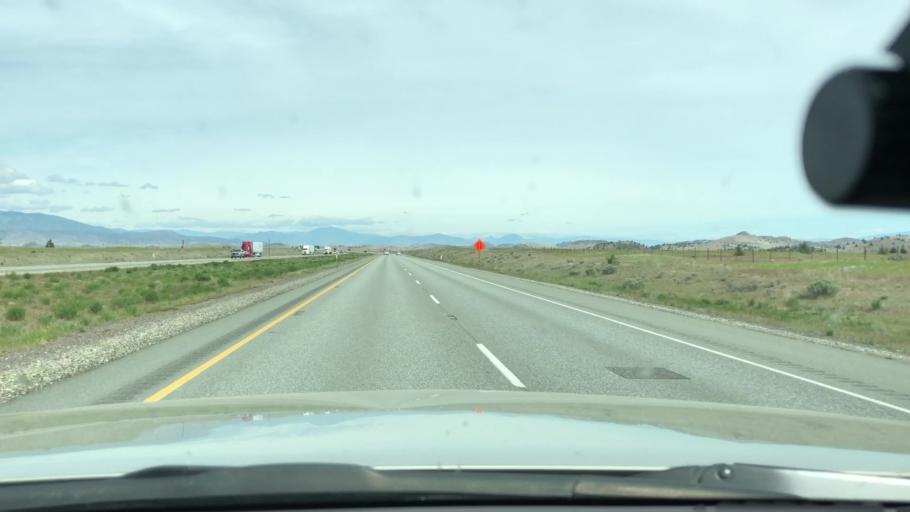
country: US
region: California
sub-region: Siskiyou County
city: Weed
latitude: 41.4597
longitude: -122.4456
